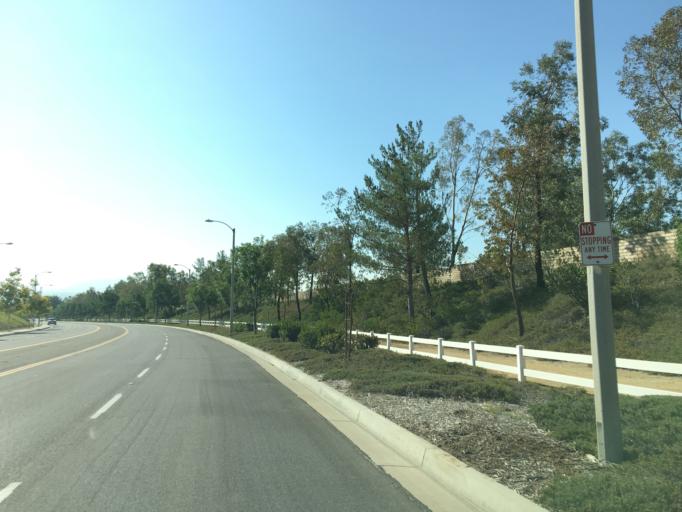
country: US
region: California
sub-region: Los Angeles County
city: Valencia
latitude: 34.4531
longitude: -118.6315
